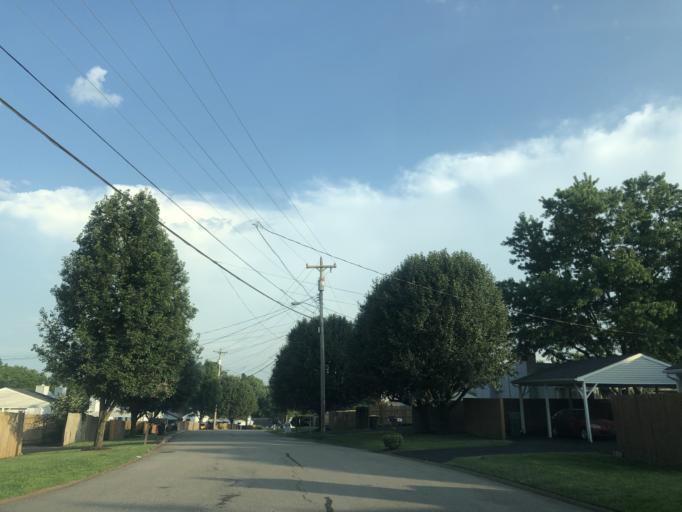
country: US
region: Tennessee
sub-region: Davidson County
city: Lakewood
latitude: 36.1448
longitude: -86.6412
